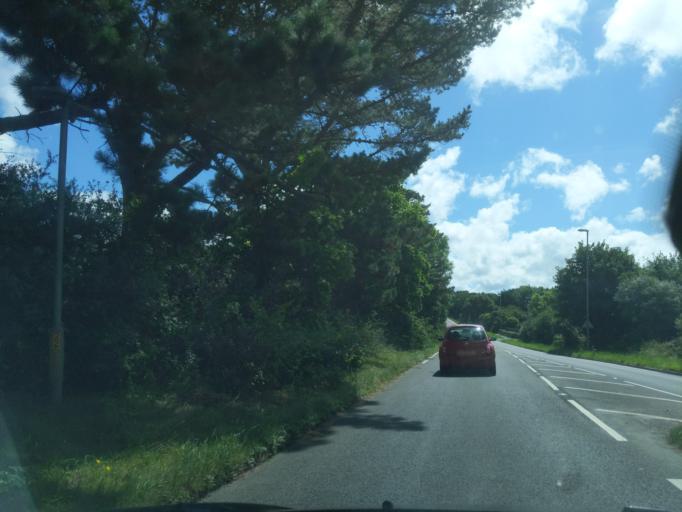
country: GB
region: England
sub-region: Cornwall
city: Marazion
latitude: 50.1453
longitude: -5.4805
